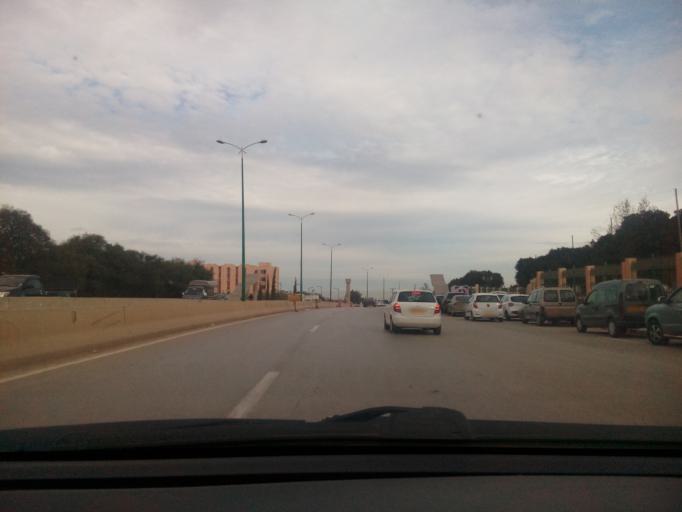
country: DZ
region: Tlemcen
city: Mansoura
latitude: 34.8958
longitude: -1.3555
